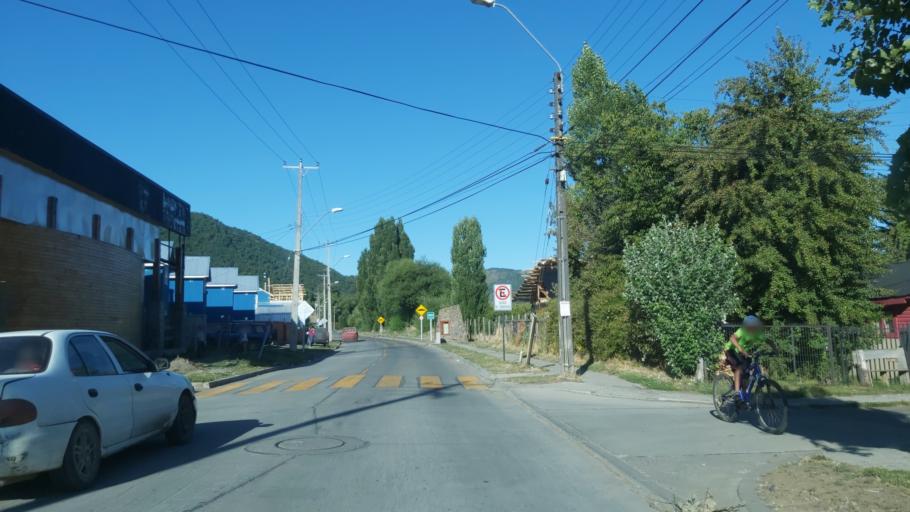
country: AR
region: Neuquen
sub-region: Departamento de Loncopue
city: Loncopue
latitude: -38.4494
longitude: -71.3692
